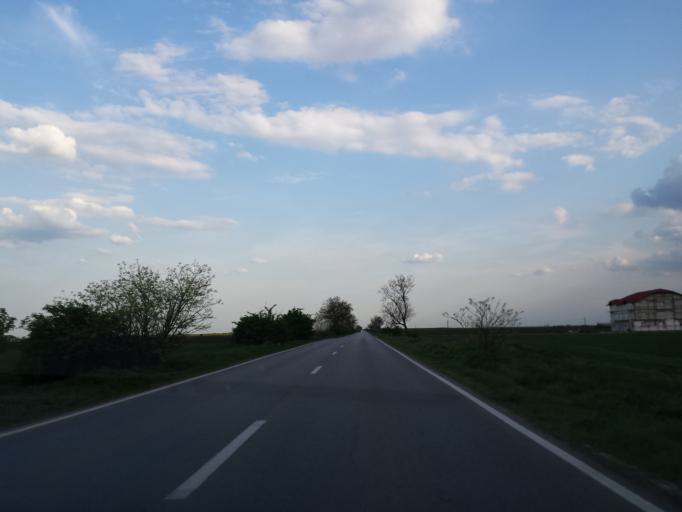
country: RO
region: Timis
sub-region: Comuna Tomnatic
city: Tomnatic
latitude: 46.0021
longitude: 20.6810
